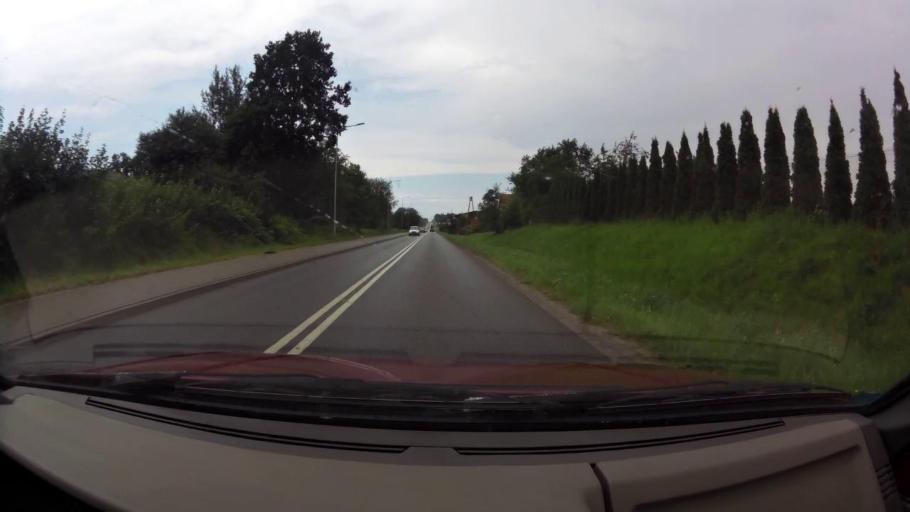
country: PL
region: West Pomeranian Voivodeship
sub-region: Koszalin
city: Koszalin
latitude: 54.1634
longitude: 16.1503
